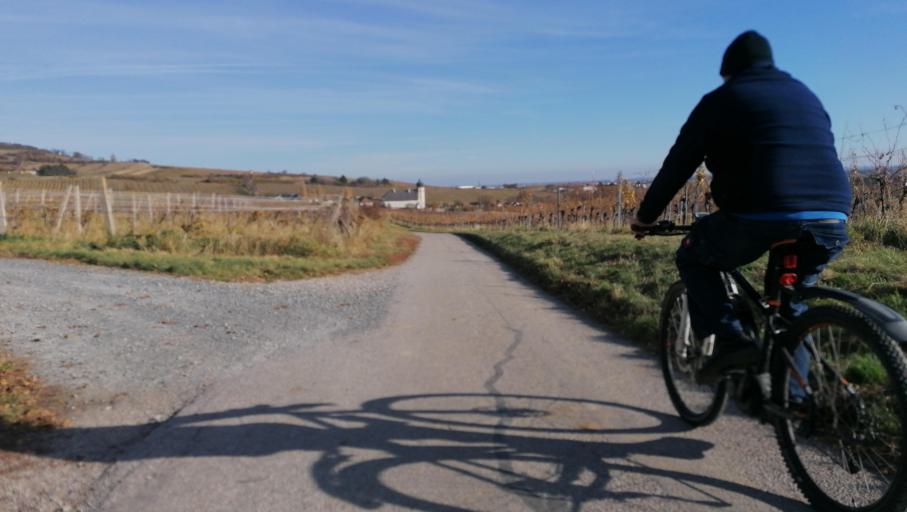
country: AT
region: Lower Austria
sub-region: Politischer Bezirk Modling
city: Gumpoldskirchen
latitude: 48.0484
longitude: 16.2867
